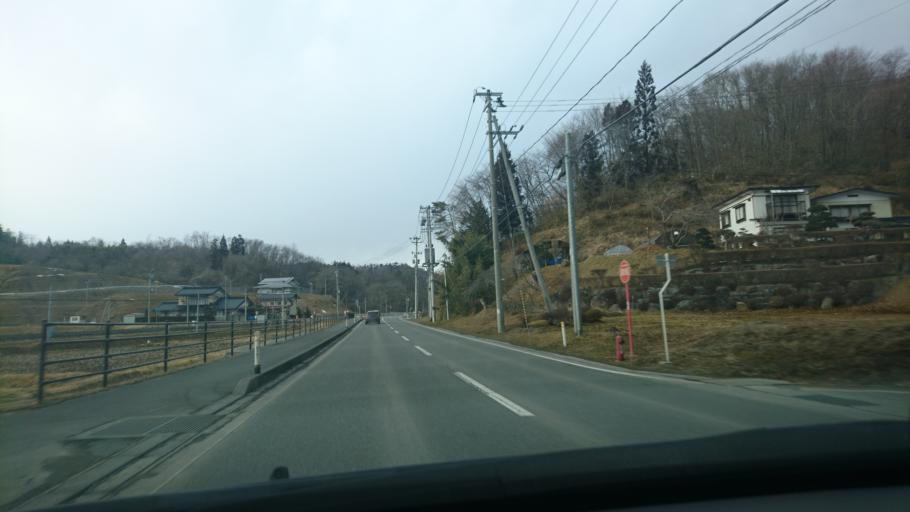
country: JP
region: Iwate
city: Ichinoseki
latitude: 38.9446
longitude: 141.3389
